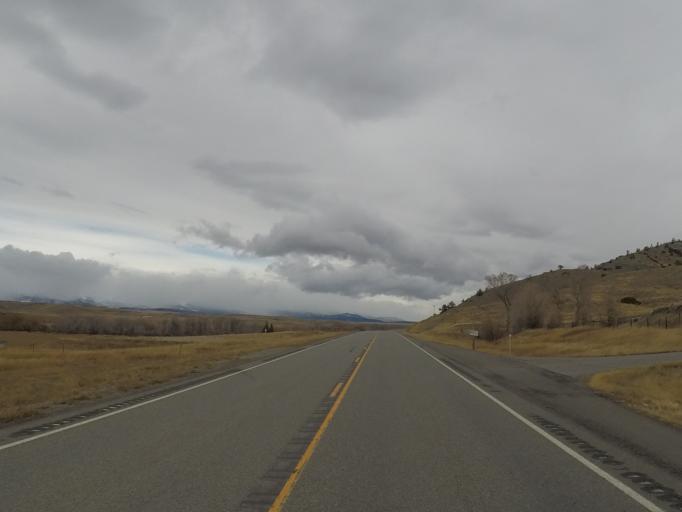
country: US
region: Montana
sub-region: Sweet Grass County
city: Big Timber
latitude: 45.8771
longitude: -109.9519
